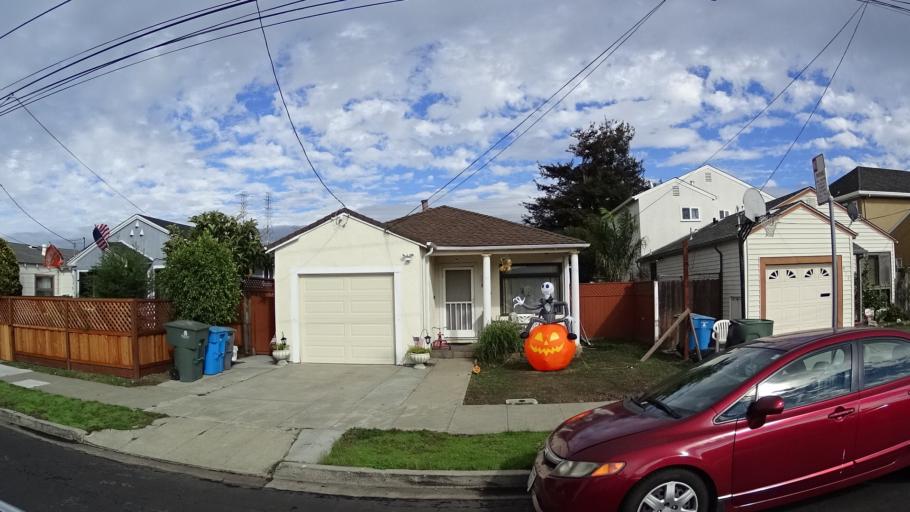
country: US
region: California
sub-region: San Mateo County
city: San Bruno
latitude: 37.6254
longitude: -122.4056
